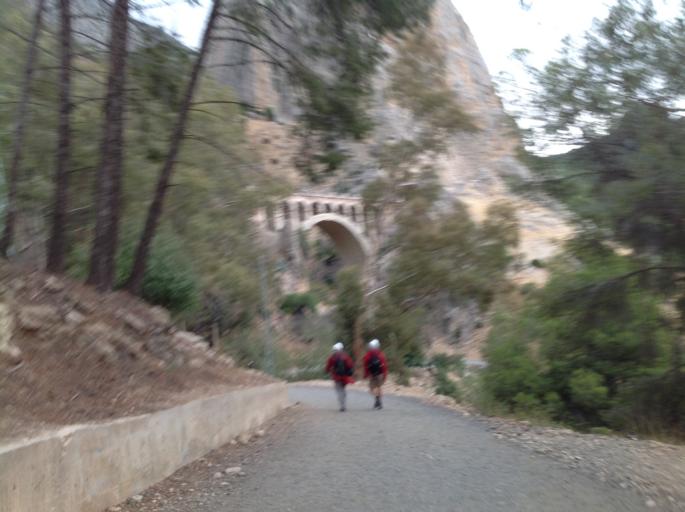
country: ES
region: Andalusia
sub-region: Provincia de Malaga
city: Carratraca
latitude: 36.9125
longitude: -4.7673
